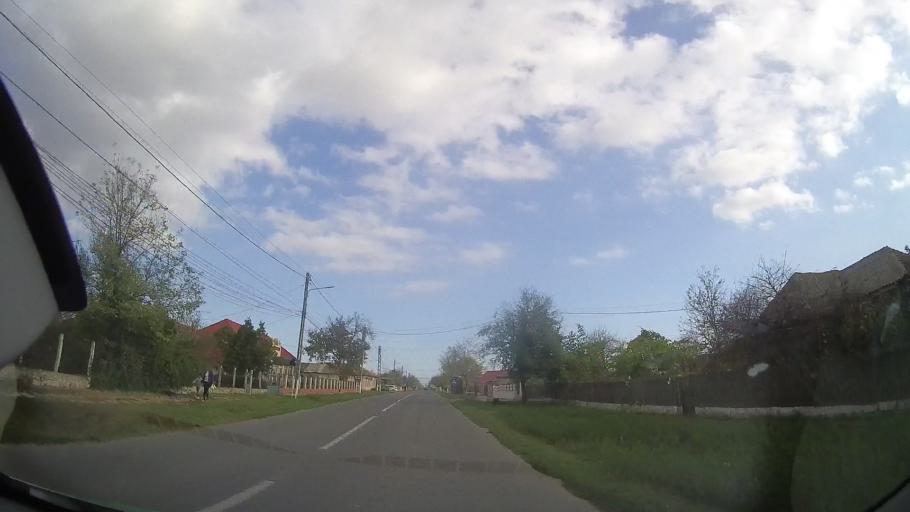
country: RO
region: Constanta
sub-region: Comuna Pecineaga
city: Pecineaga
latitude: 43.8951
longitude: 28.5023
